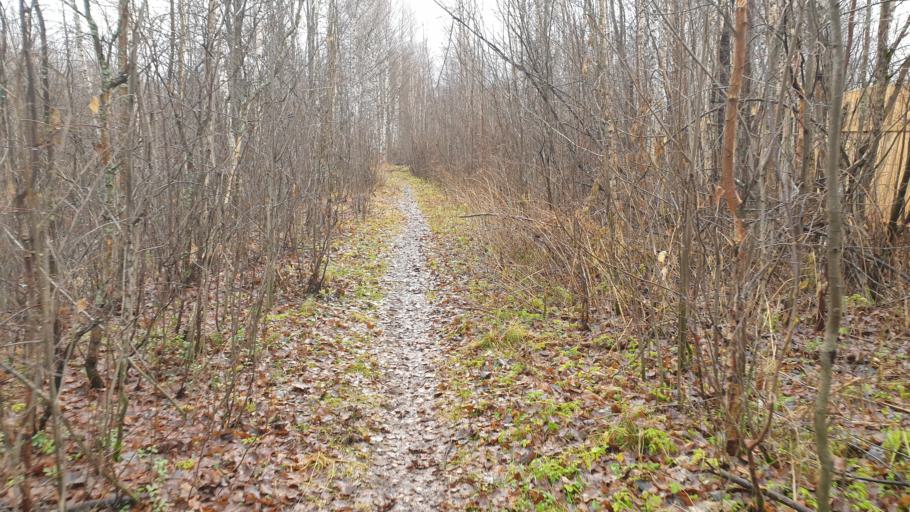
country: RU
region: Kirov
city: Kirs
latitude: 59.3339
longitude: 52.2386
